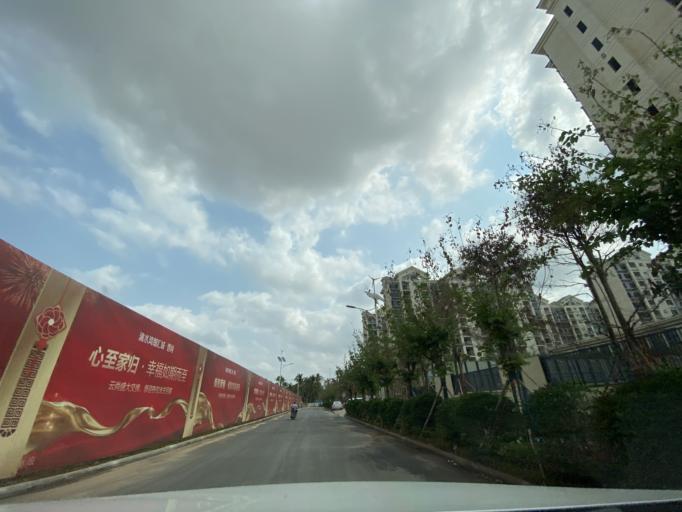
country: CN
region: Hainan
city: Yingzhou
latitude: 18.4088
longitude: 109.8557
